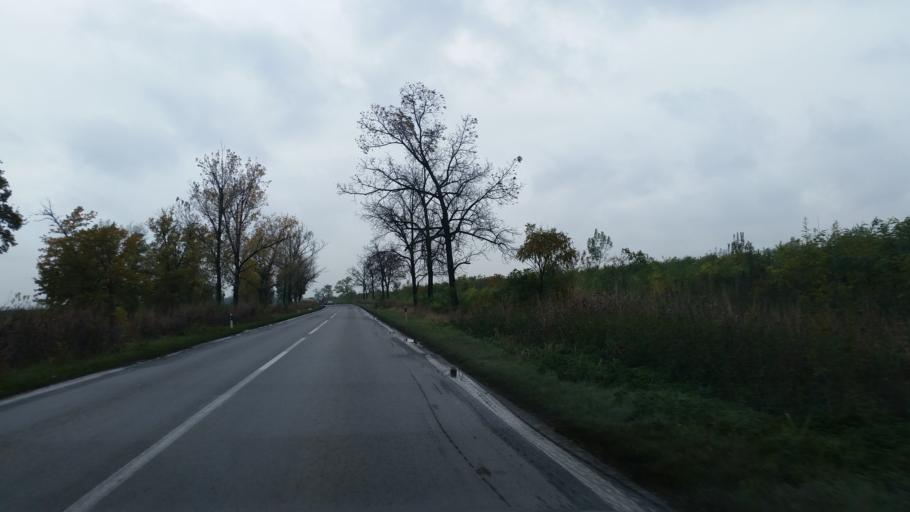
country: RS
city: Ecka
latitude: 45.3390
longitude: 20.4325
